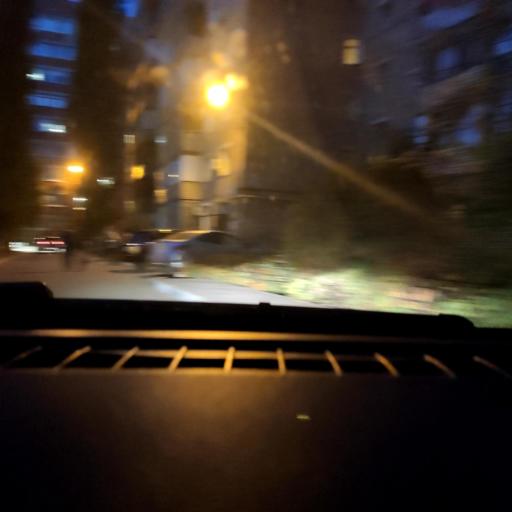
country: RU
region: Voronezj
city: Voronezh
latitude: 51.6430
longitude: 39.2759
